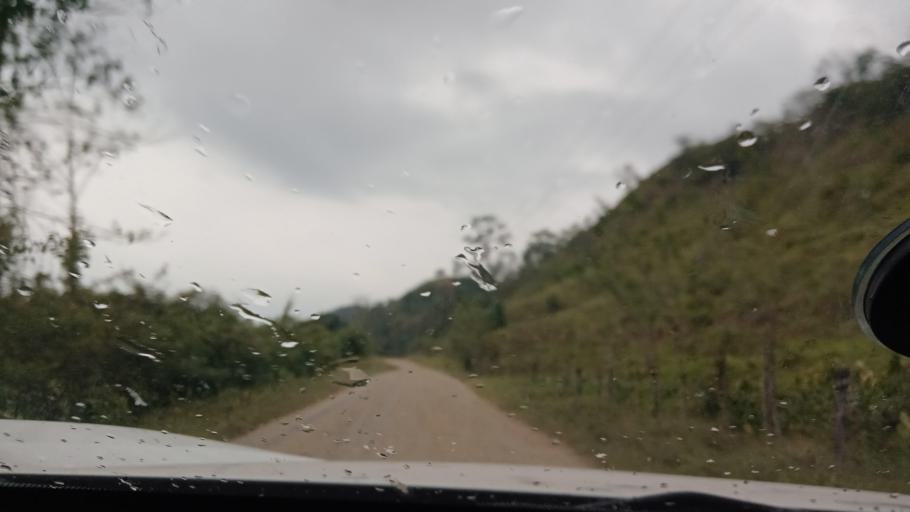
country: MX
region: Veracruz
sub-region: Uxpanapa
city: Poblado 10
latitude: 17.4518
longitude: -94.0864
